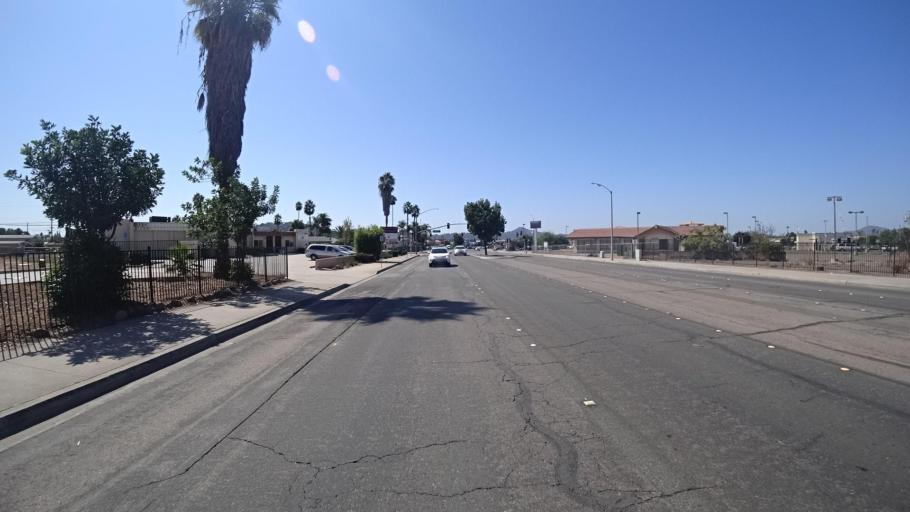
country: US
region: California
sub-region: San Diego County
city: Bostonia
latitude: 32.7972
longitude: -116.9336
